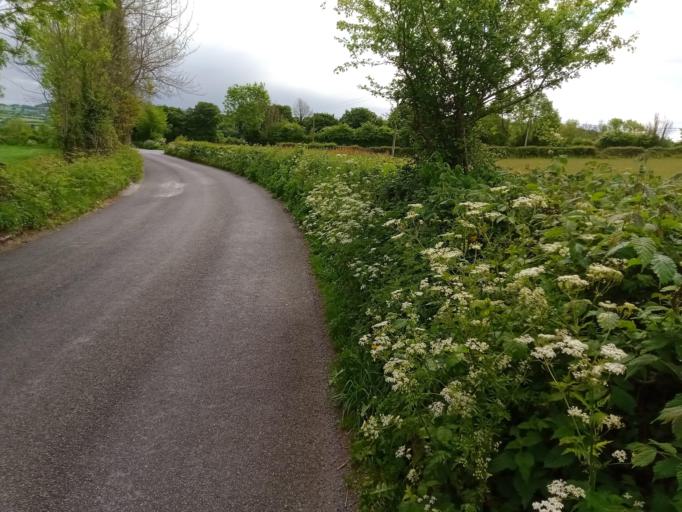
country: IE
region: Leinster
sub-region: Kilkenny
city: Thomastown
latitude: 52.4995
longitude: -7.1265
